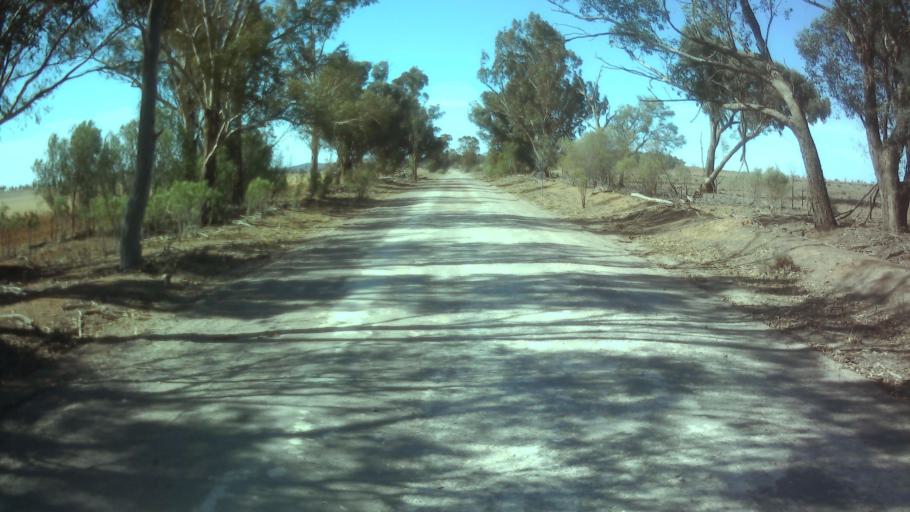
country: AU
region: New South Wales
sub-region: Forbes
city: Forbes
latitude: -33.7211
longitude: 147.7455
